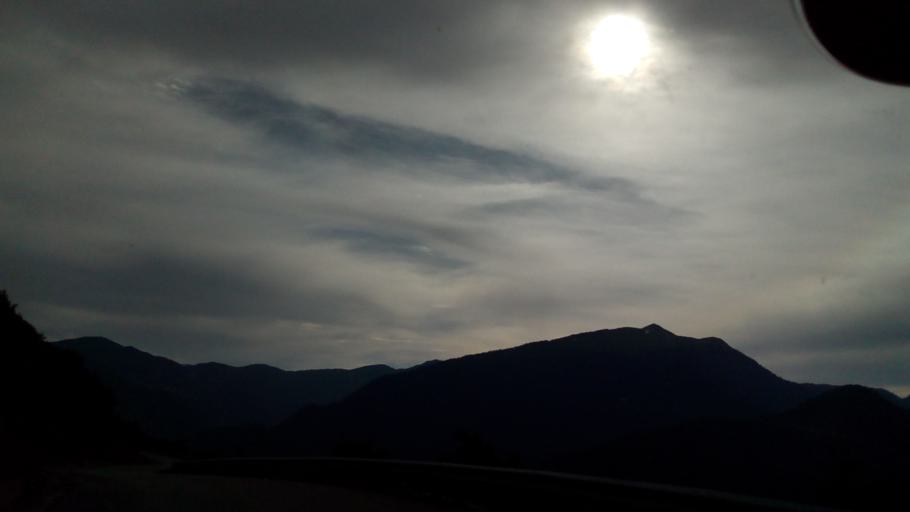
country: GR
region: West Greece
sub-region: Nomos Aitolias kai Akarnanias
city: Thermo
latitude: 38.6806
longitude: 21.8765
